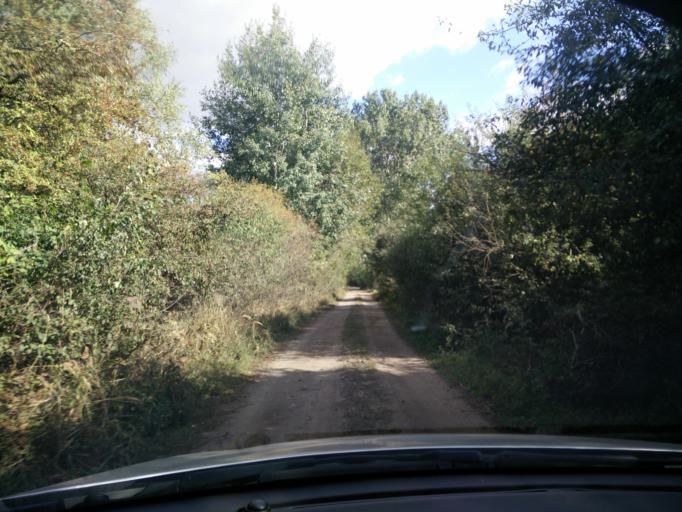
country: PL
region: Greater Poland Voivodeship
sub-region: Powiat sredzki
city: Sroda Wielkopolska
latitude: 52.2805
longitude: 17.2513
